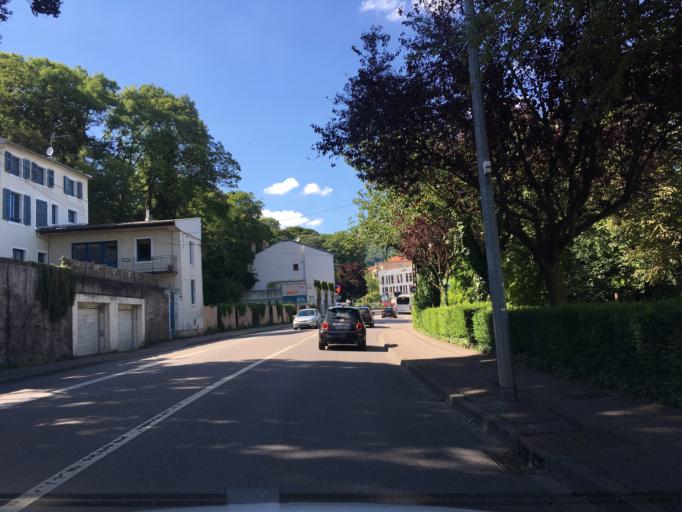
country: FR
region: Lorraine
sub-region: Departement de Meurthe-et-Moselle
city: Maxeville
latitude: 48.7065
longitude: 6.1675
